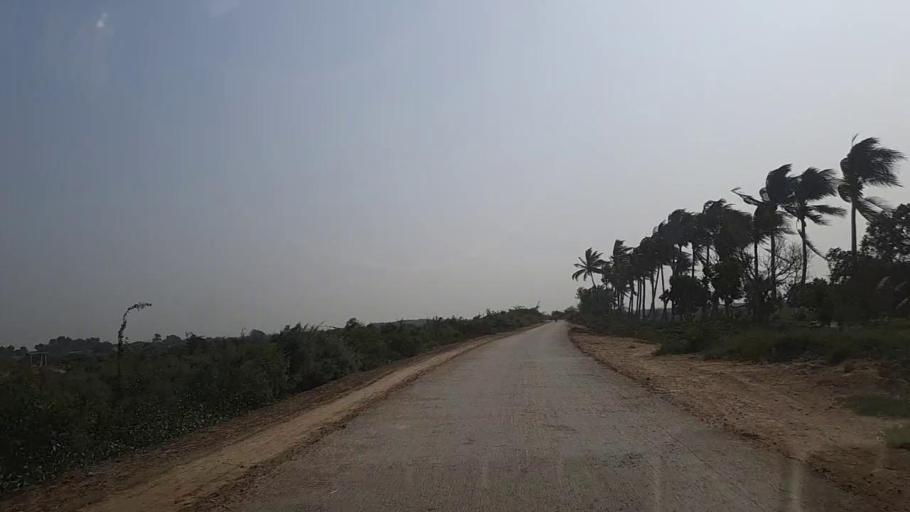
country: PK
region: Sindh
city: Keti Bandar
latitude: 24.2434
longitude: 67.6366
